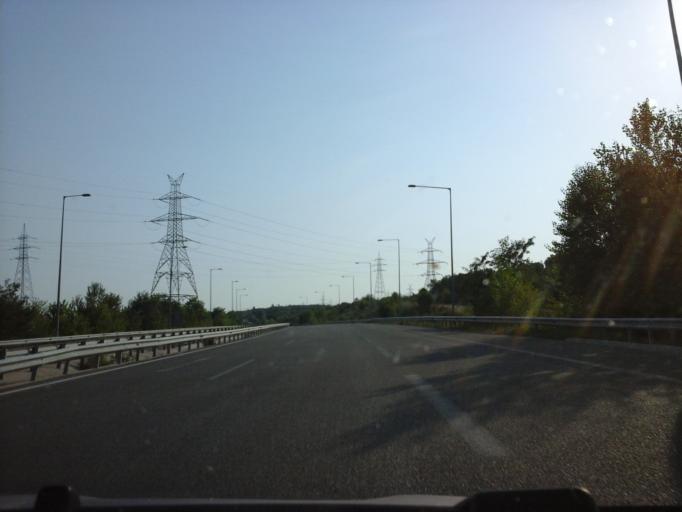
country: GR
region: East Macedonia and Thrace
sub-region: Nomos Xanthis
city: Petrochori
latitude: 41.0678
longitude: 24.7493
